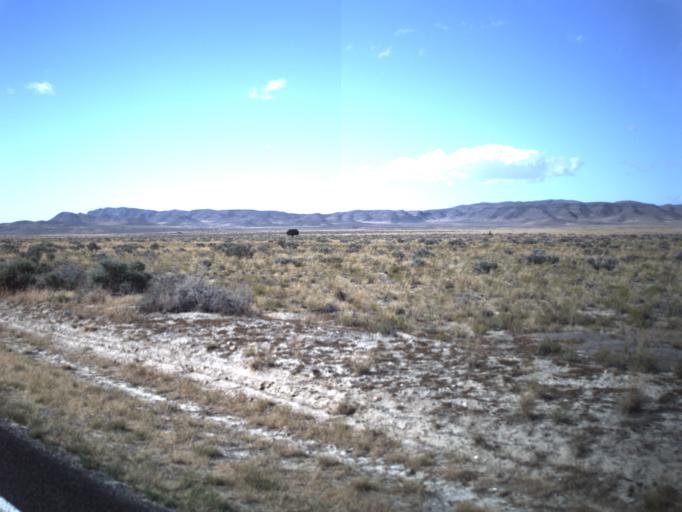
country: US
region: Utah
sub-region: Millard County
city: Delta
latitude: 38.9318
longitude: -112.8097
